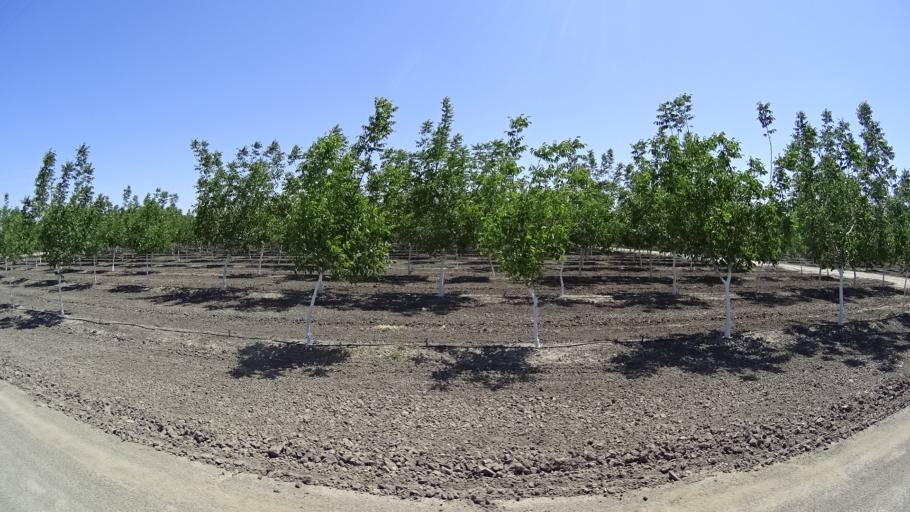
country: US
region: California
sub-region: Kings County
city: Armona
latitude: 36.2440
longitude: -119.7267
